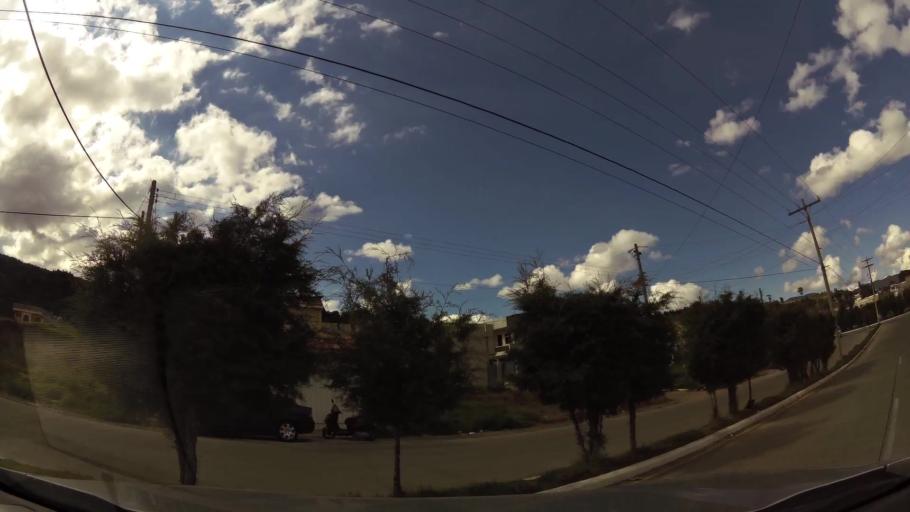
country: GT
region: Quetzaltenango
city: Quetzaltenango
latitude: 14.8343
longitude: -91.5494
